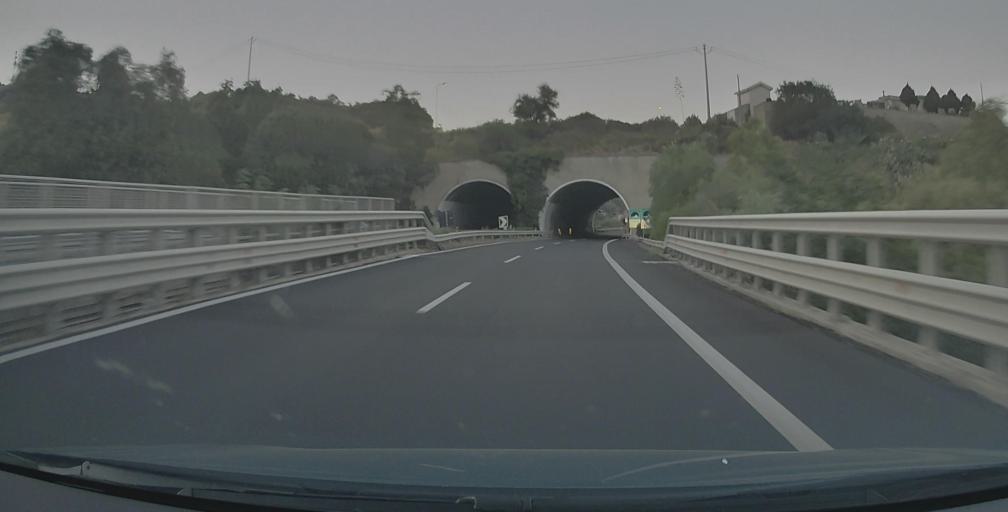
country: IT
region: Sicily
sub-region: Messina
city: Sant'Alessio Siculo
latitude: 37.9219
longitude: 15.3443
